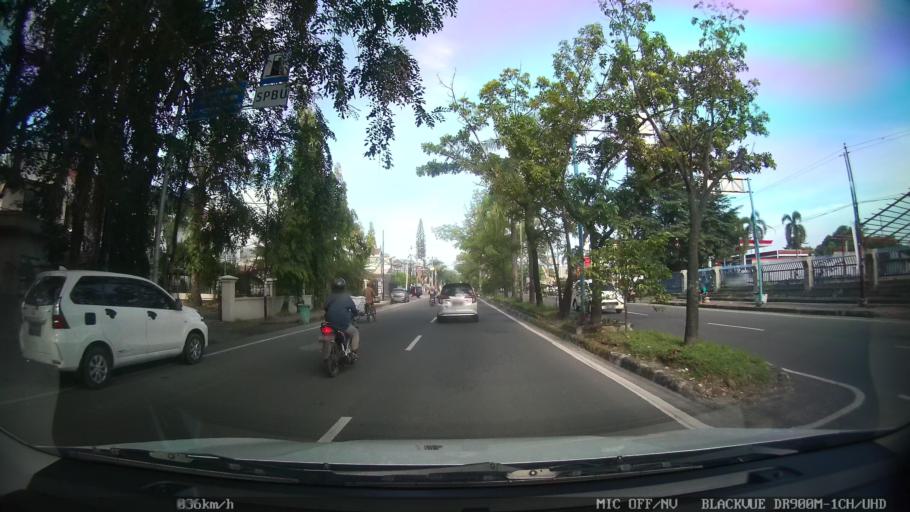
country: ID
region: North Sumatra
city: Medan
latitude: 3.6077
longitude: 98.6534
